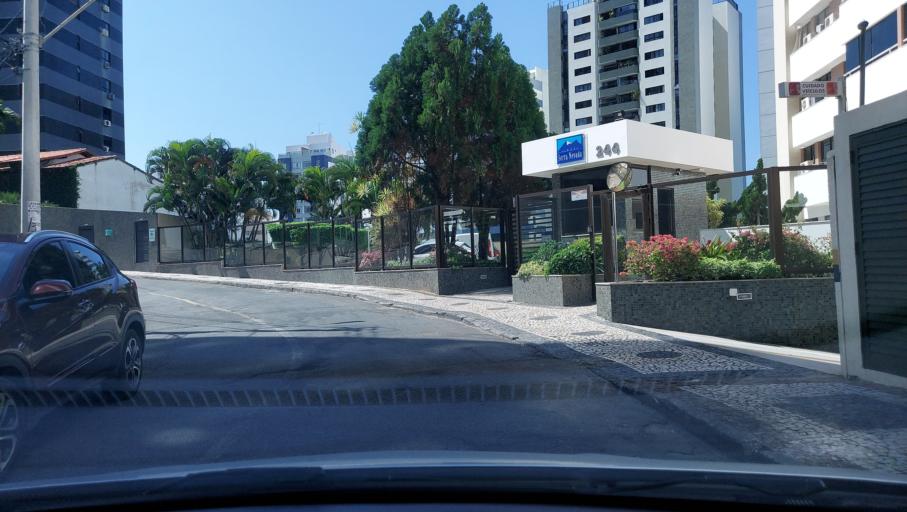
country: BR
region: Bahia
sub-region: Salvador
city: Salvador
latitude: -12.9881
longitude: -38.4629
